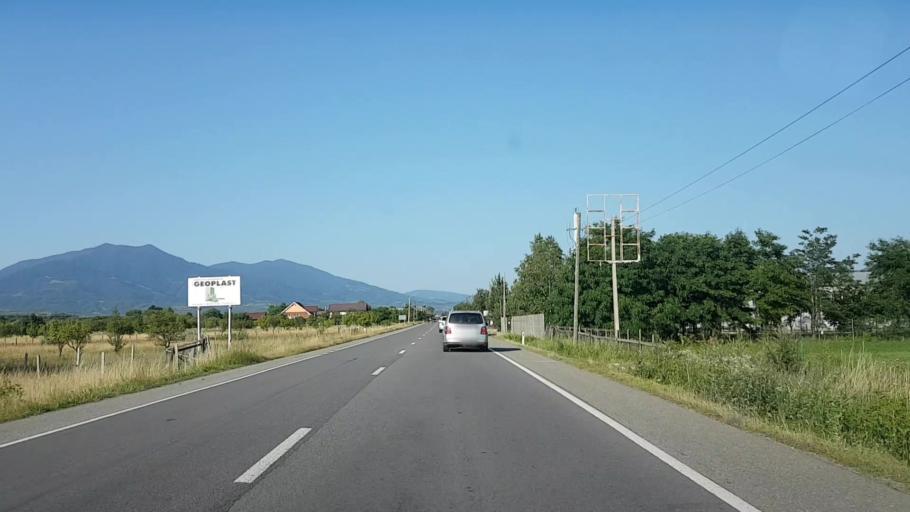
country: RO
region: Bistrita-Nasaud
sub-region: Comuna Livezile
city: Livezile
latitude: 47.1959
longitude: 24.6247
